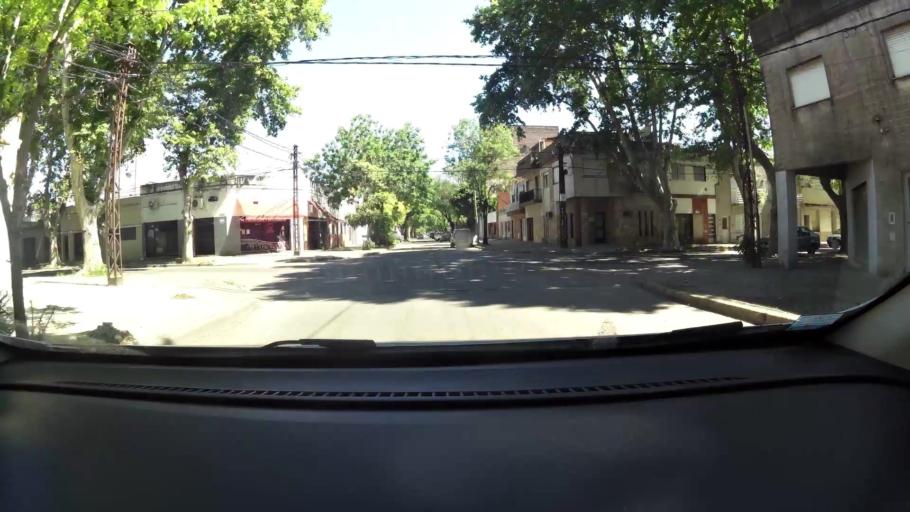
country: AR
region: Santa Fe
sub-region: Departamento de Rosario
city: Rosario
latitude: -32.9412
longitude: -60.6824
